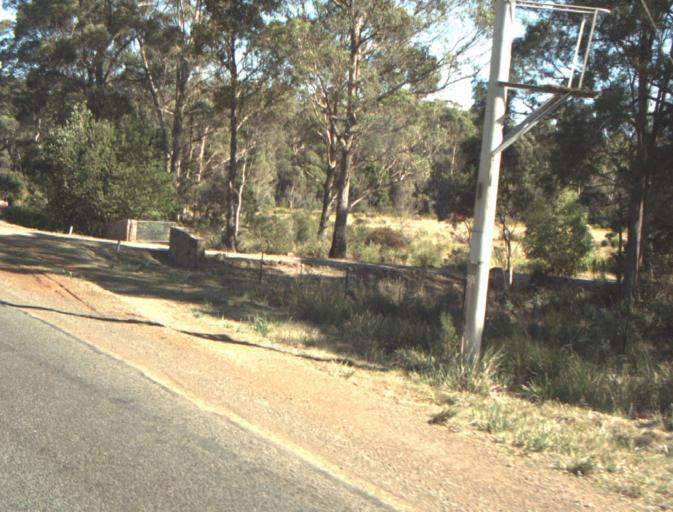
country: AU
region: Tasmania
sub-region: Launceston
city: Mayfield
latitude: -41.3028
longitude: 147.1334
